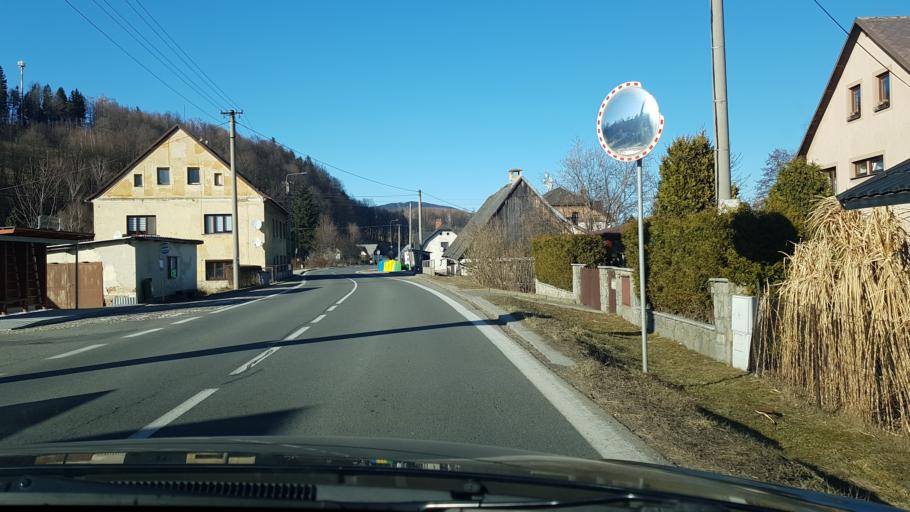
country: CZ
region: Olomoucky
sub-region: Okres Jesenik
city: Jesenik
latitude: 50.2047
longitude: 17.1964
